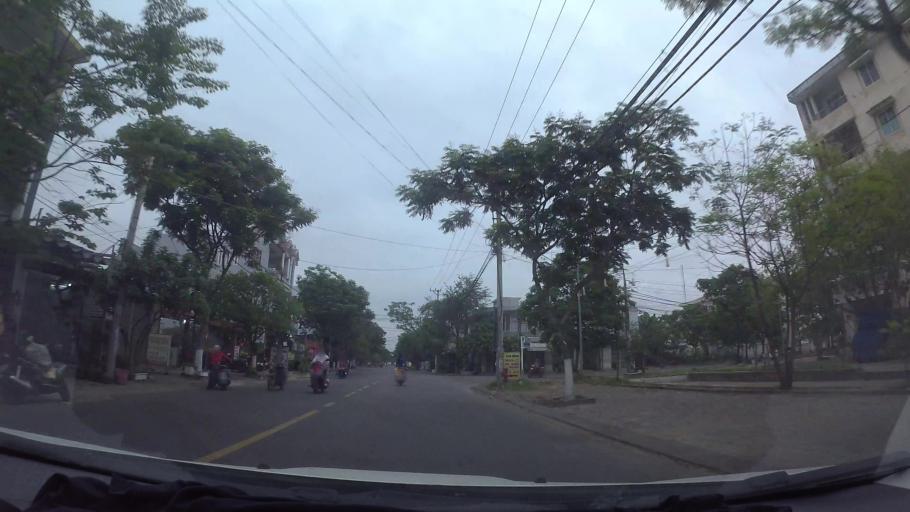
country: VN
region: Da Nang
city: Lien Chieu
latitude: 16.0724
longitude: 108.1566
